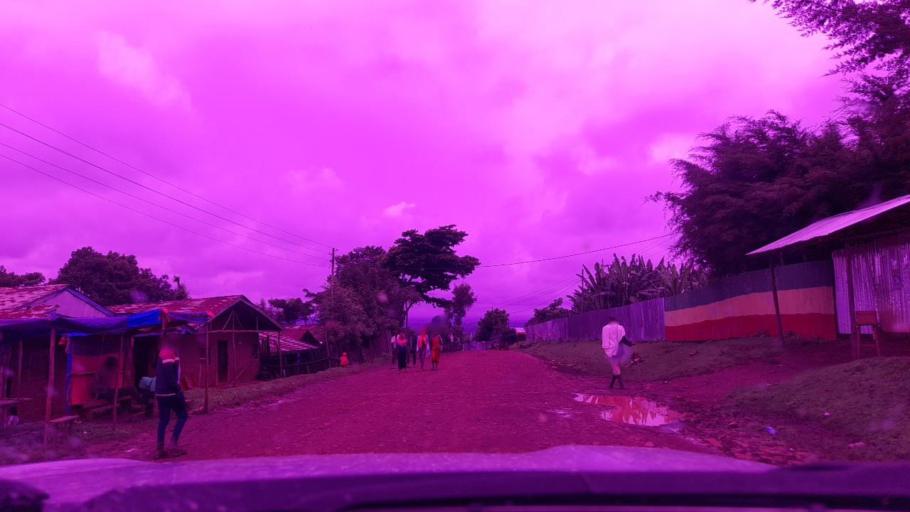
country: ET
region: Southern Nations, Nationalities, and People's Region
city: Tippi
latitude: 7.5933
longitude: 35.7513
